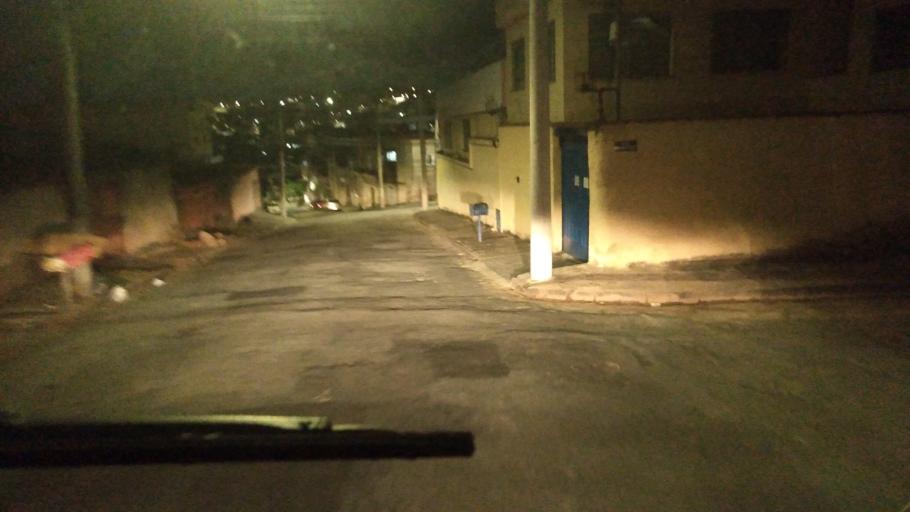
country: BR
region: Minas Gerais
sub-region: Belo Horizonte
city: Belo Horizonte
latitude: -19.8758
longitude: -43.9379
